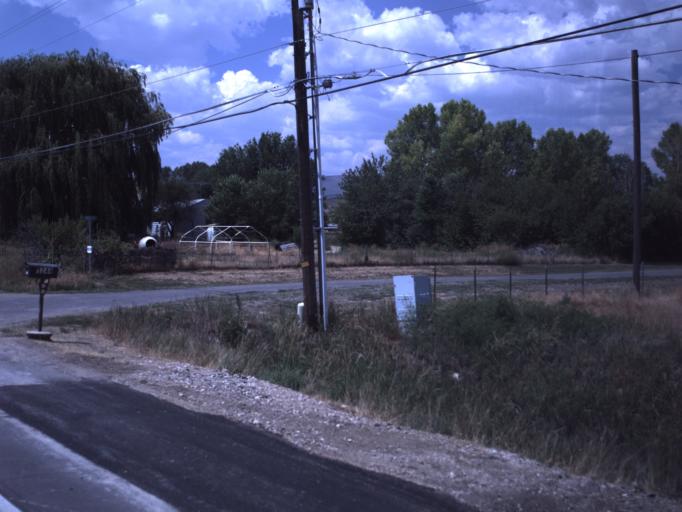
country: US
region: Utah
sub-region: Uintah County
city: Maeser
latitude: 40.4627
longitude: -109.5904
